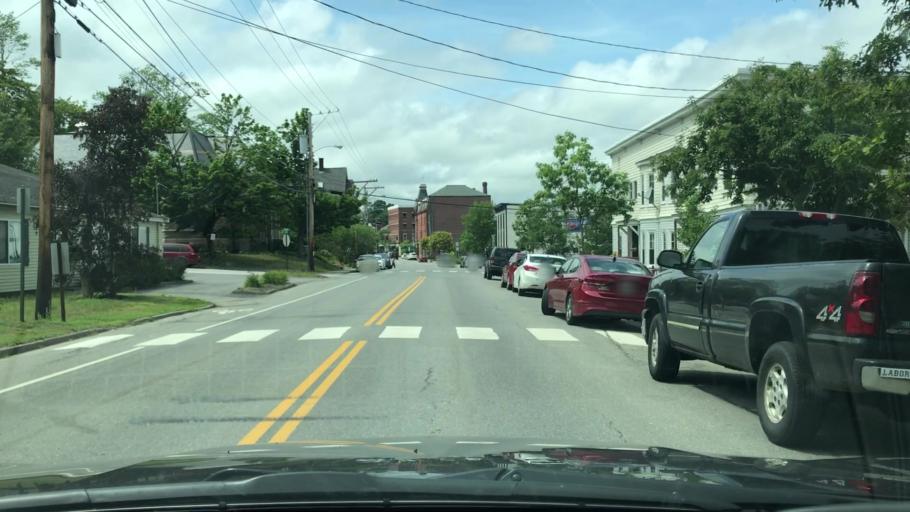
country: US
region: Maine
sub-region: Waldo County
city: Belfast
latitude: 44.4249
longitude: -69.0040
